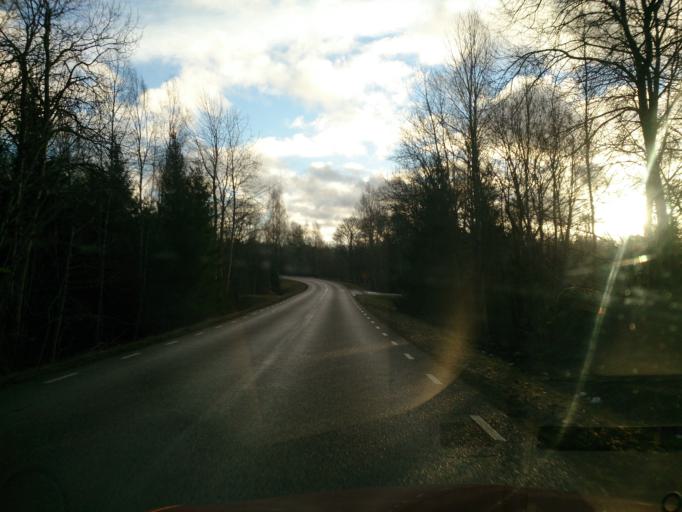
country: SE
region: OEstergoetland
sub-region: Atvidabergs Kommun
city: Atvidaberg
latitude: 58.2681
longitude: 16.0336
